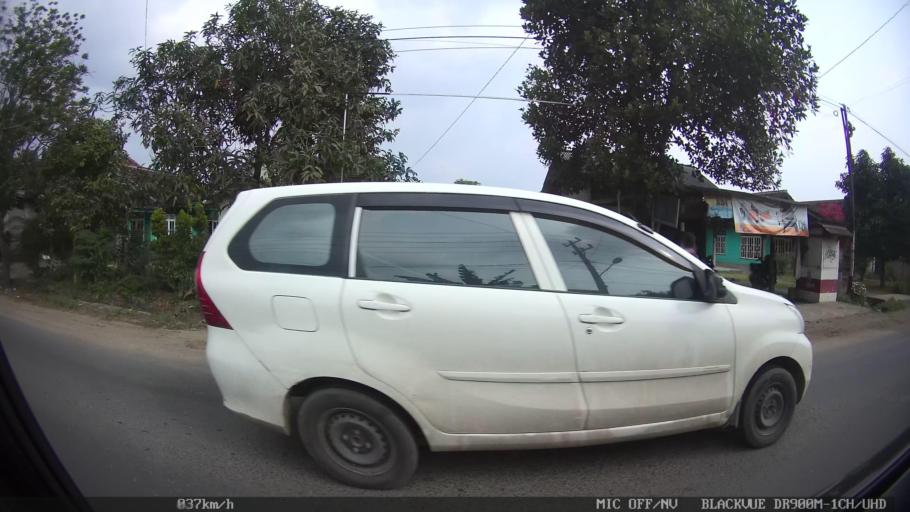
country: ID
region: Lampung
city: Gadingrejo
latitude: -5.3762
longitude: 105.0376
